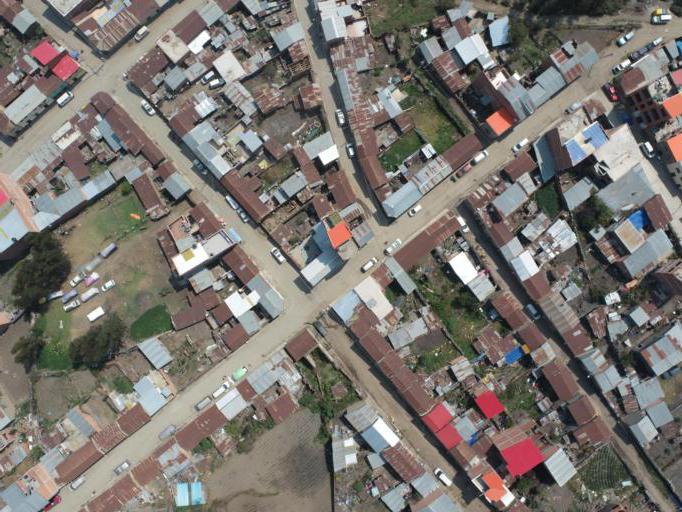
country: BO
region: La Paz
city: Quime
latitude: -16.9828
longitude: -67.2159
